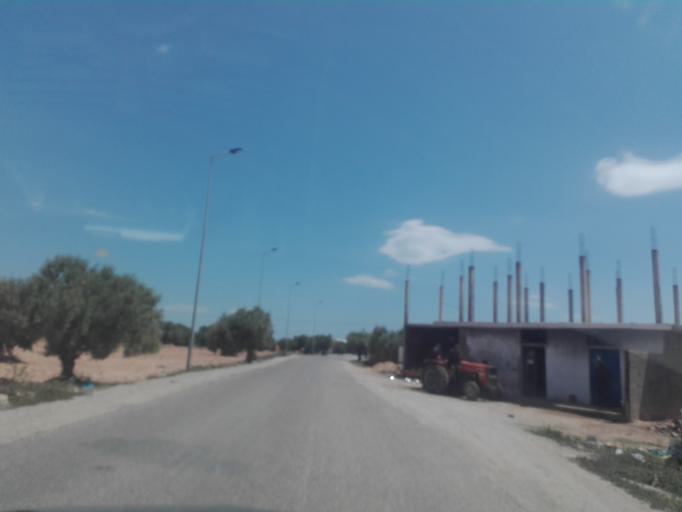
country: TN
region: Safaqis
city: Sfax
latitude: 34.6246
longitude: 10.6028
